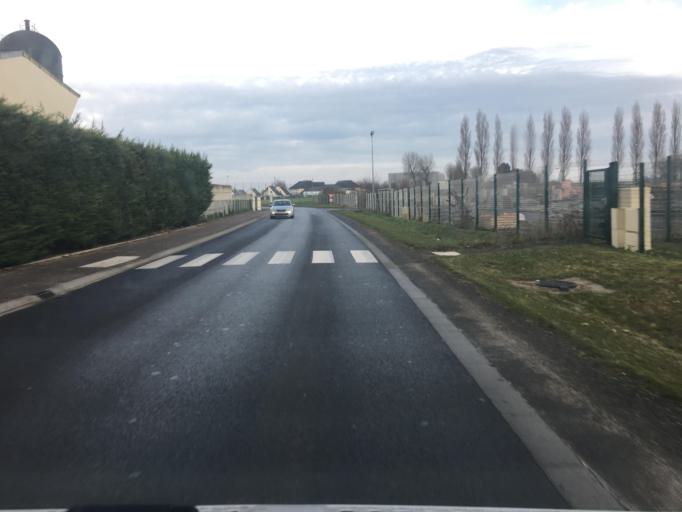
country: FR
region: Lower Normandy
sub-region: Departement du Calvados
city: Creully
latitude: 49.2757
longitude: -0.5457
